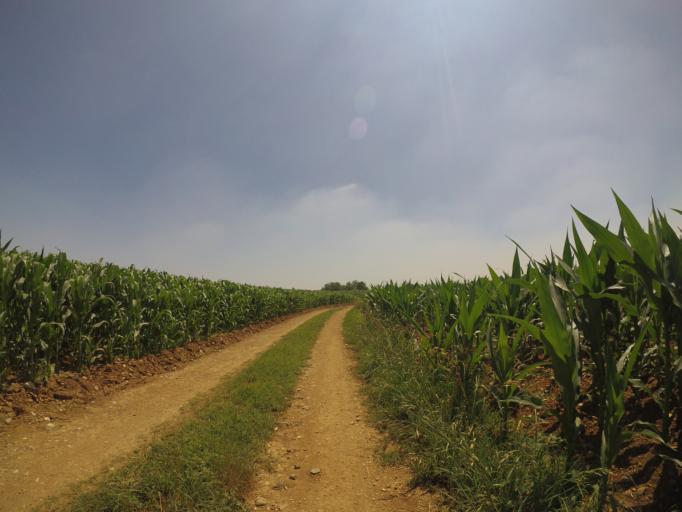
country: IT
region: Friuli Venezia Giulia
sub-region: Provincia di Udine
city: Bertiolo
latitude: 45.9473
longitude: 13.0284
